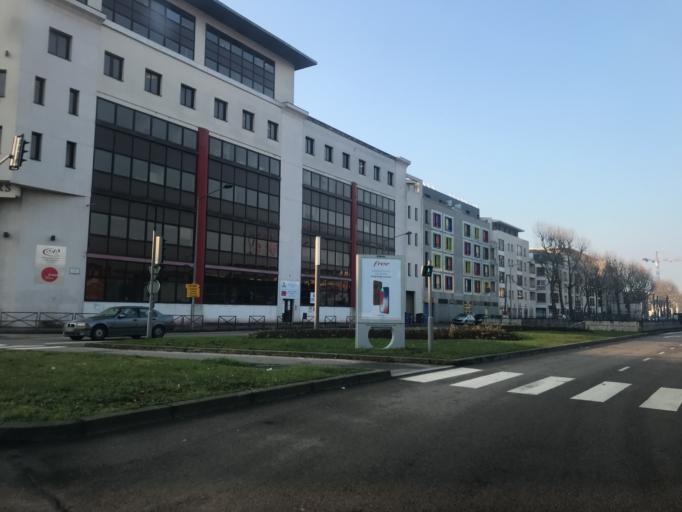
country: FR
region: Haute-Normandie
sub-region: Departement de la Seine-Maritime
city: Sotteville-les-Rouen
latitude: 49.4307
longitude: 1.0786
